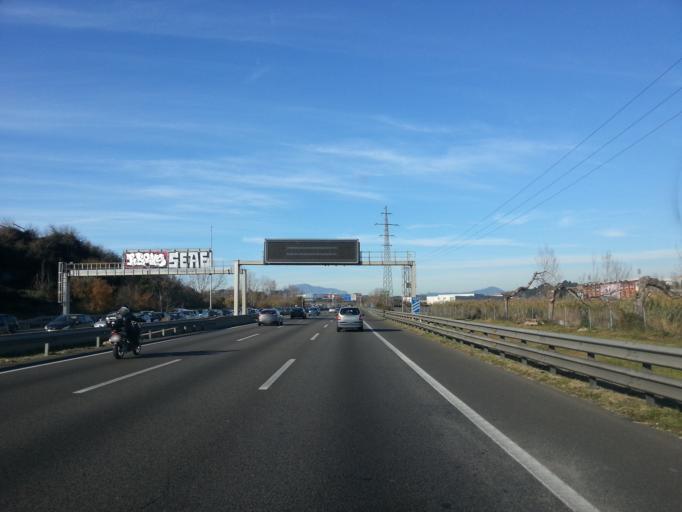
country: ES
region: Catalonia
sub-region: Provincia de Barcelona
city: Ripollet
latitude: 41.4961
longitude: 2.1491
